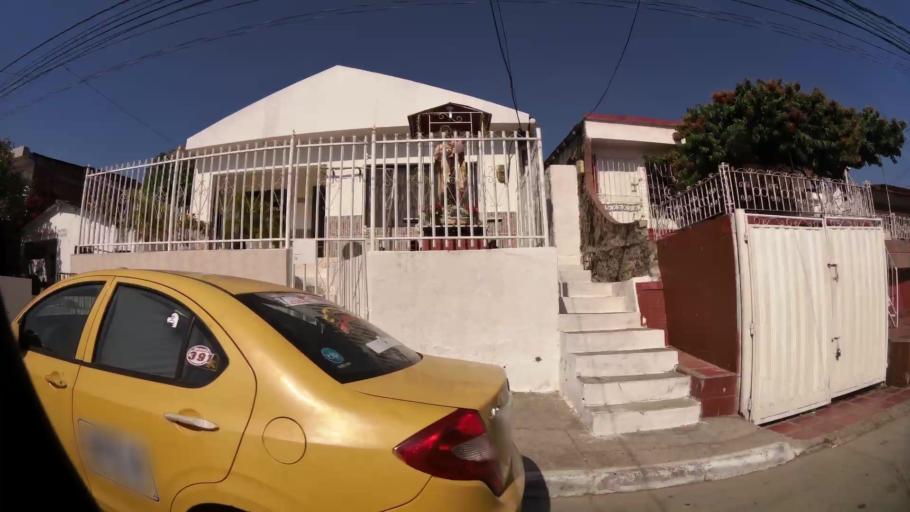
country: CO
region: Bolivar
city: Cartagena
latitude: 10.3993
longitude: -75.4972
